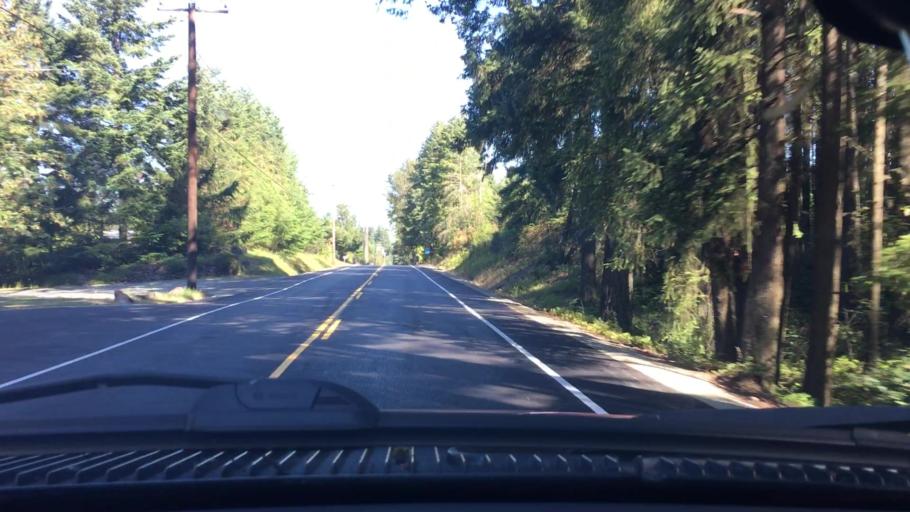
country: US
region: Washington
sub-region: King County
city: Lake Morton-Berrydale
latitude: 47.3214
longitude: -122.1070
